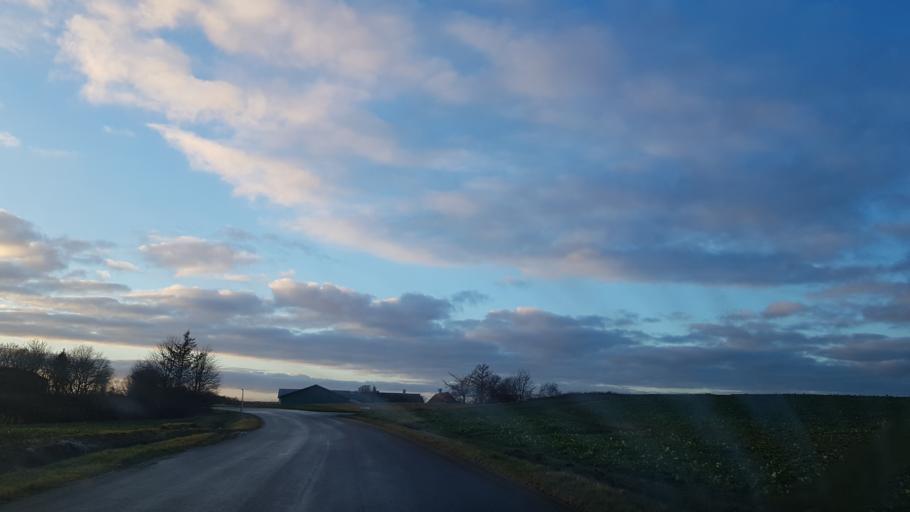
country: DK
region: South Denmark
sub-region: Kolding Kommune
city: Vamdrup
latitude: 55.3741
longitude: 9.2994
